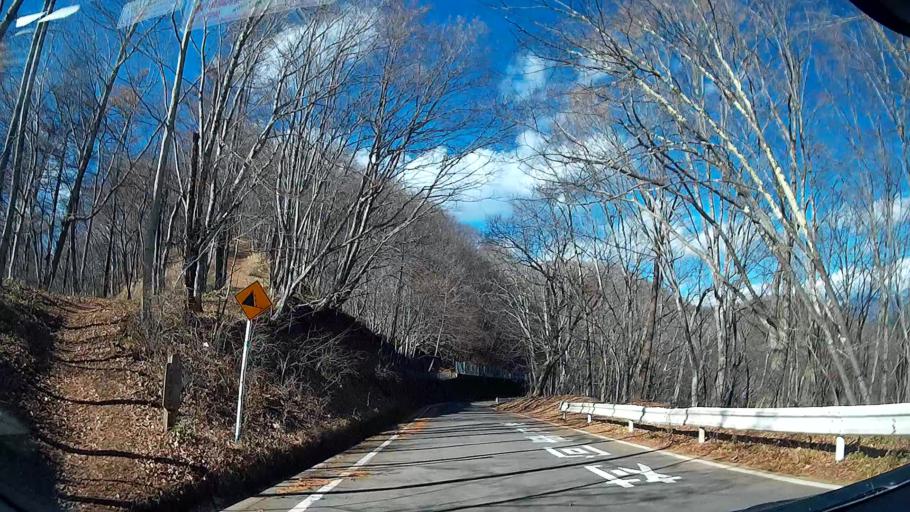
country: JP
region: Yamanashi
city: Otsuki
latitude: 35.7278
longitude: 138.9495
